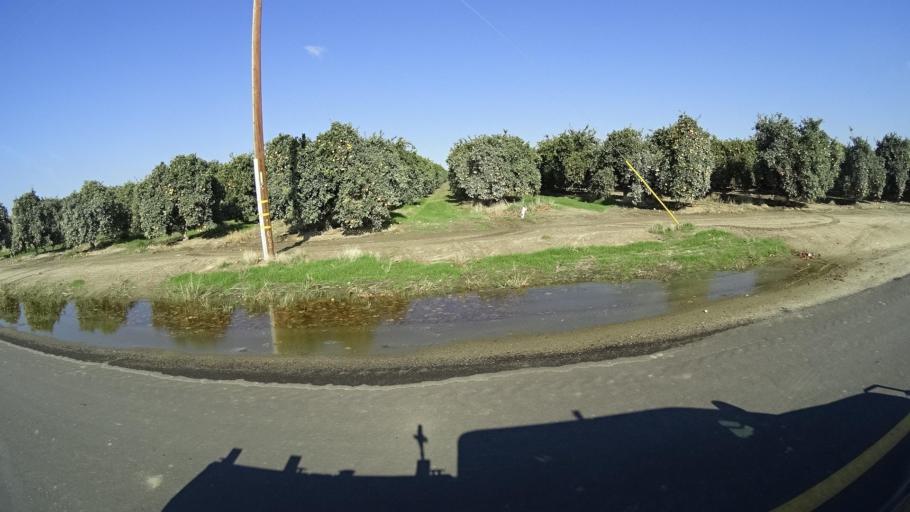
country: US
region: California
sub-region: Kern County
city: Arvin
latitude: 35.2675
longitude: -118.7799
